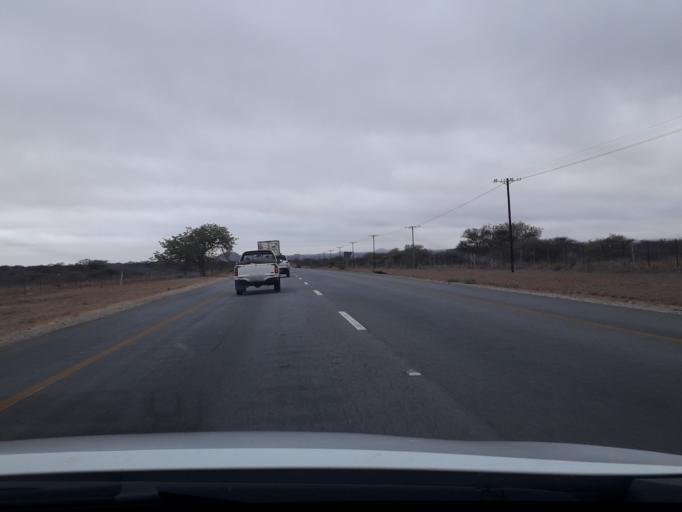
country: ZA
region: Limpopo
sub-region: Capricorn District Municipality
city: Mankoeng
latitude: -23.5758
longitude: 29.6726
